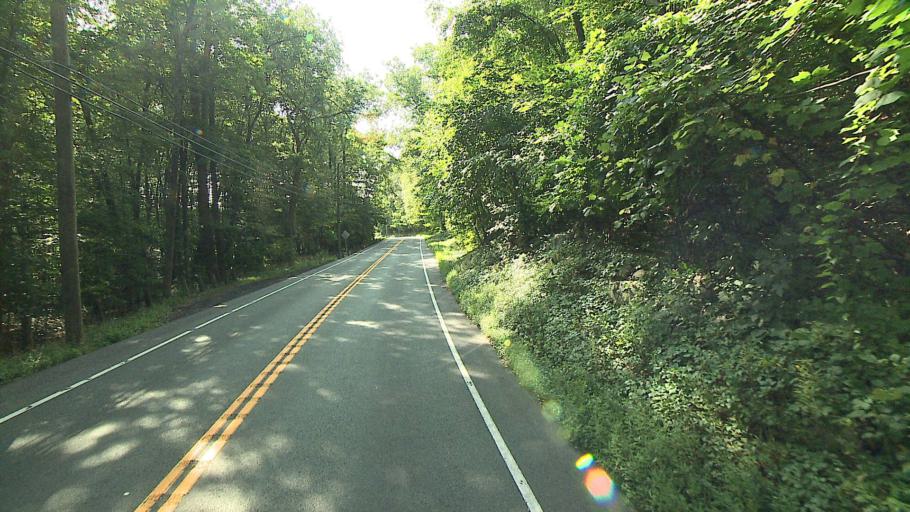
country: US
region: Connecticut
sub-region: Fairfield County
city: Sherman
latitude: 41.6146
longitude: -73.4534
